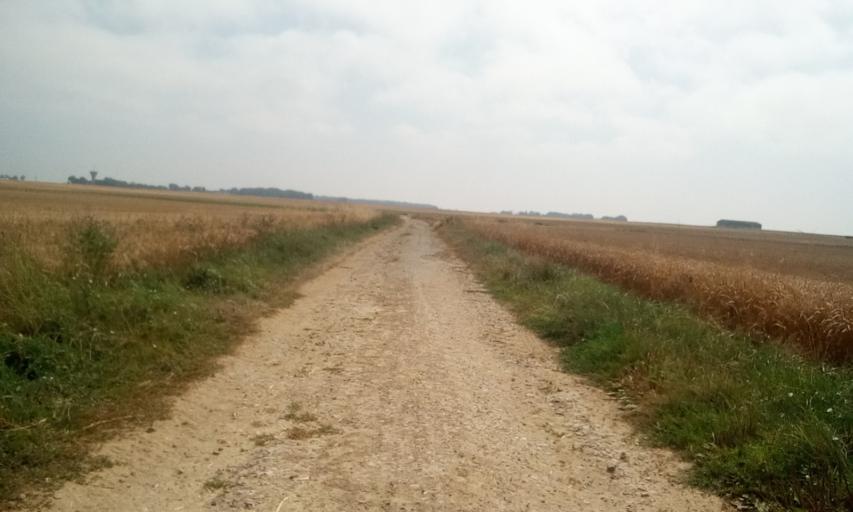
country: FR
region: Lower Normandy
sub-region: Departement du Calvados
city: Bernieres-sur-Mer
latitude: 49.3257
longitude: -0.4110
